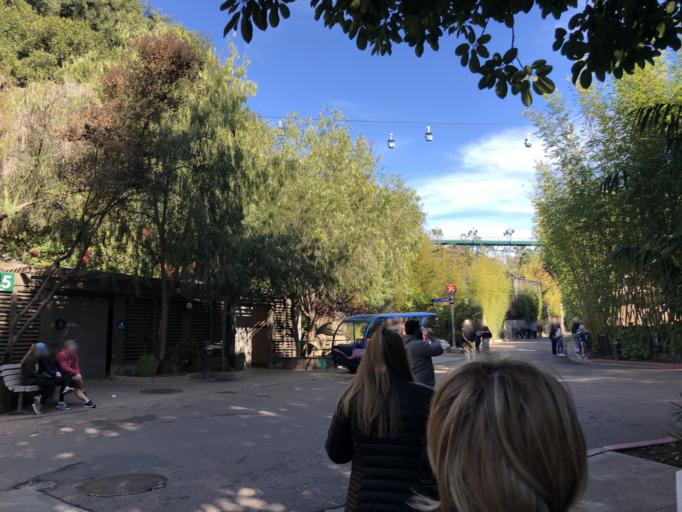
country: US
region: California
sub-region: San Diego County
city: San Diego
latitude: 32.7339
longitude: -117.1535
